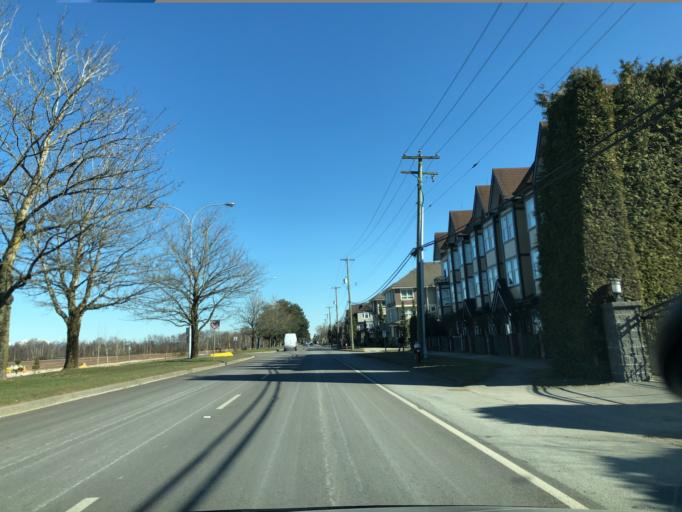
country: CA
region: British Columbia
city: Richmond
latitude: 49.1701
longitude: -123.1208
